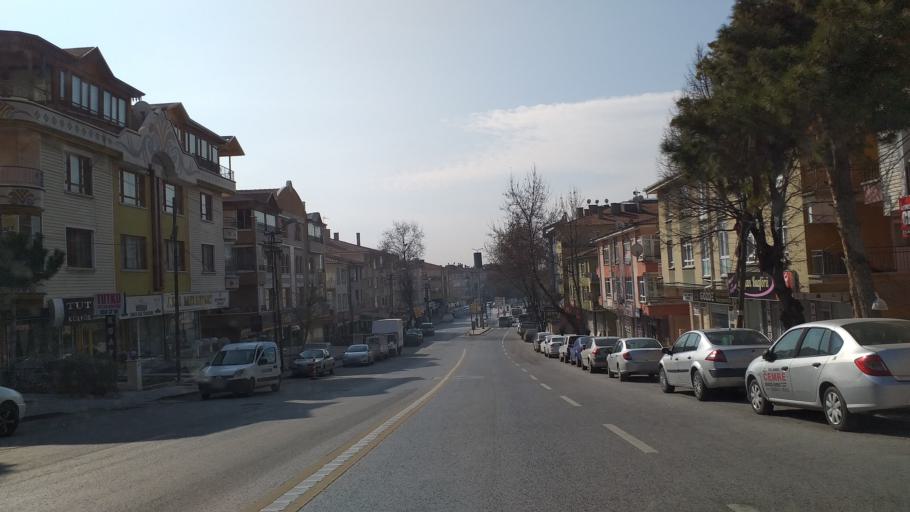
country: TR
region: Ankara
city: Ankara
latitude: 39.9859
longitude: 32.8543
